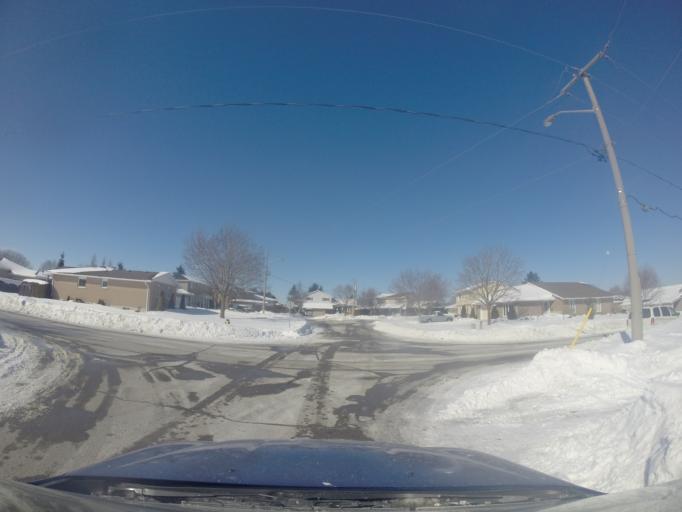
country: CA
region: Ontario
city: Omemee
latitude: 44.3410
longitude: -78.7497
